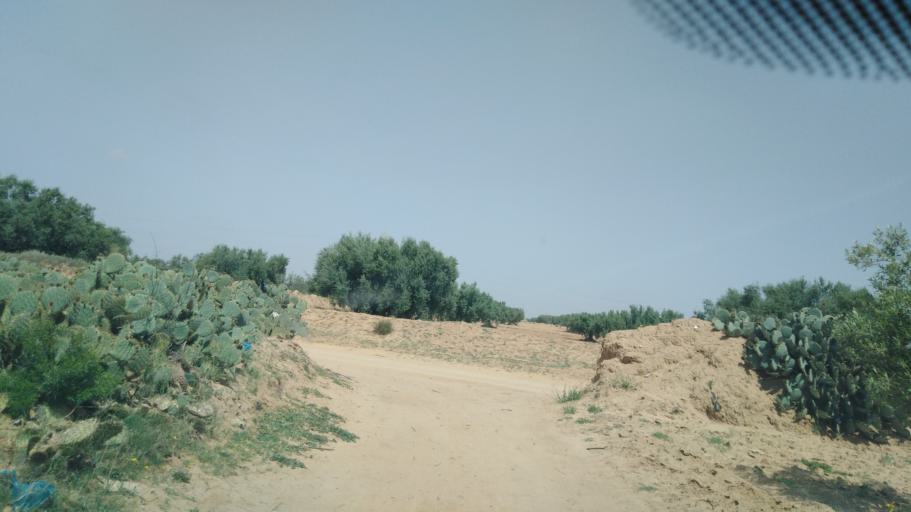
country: TN
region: Safaqis
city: Sfax
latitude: 34.7381
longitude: 10.5728
